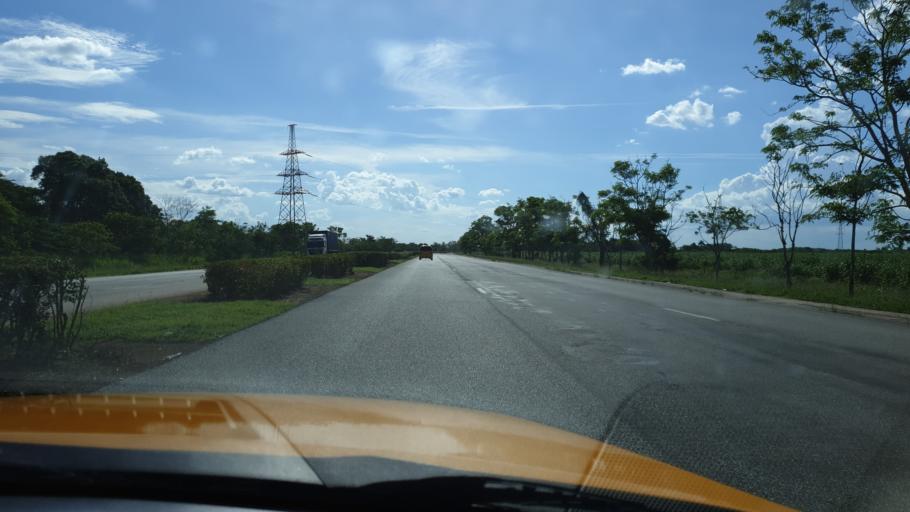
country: CU
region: Cienfuegos
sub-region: Municipio de Aguada de Pasajeros
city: Aguada de Pasajeros
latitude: 22.4086
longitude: -80.8849
